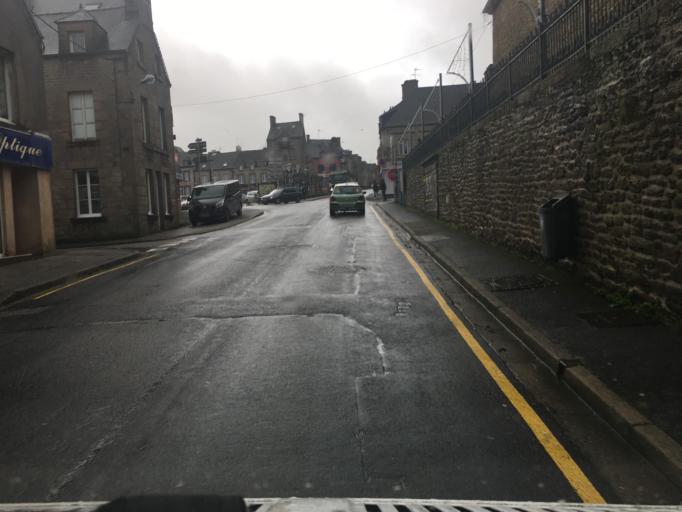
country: FR
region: Lower Normandy
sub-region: Departement de la Manche
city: Saint-Pierre-Eglise
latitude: 49.6689
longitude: -1.4053
